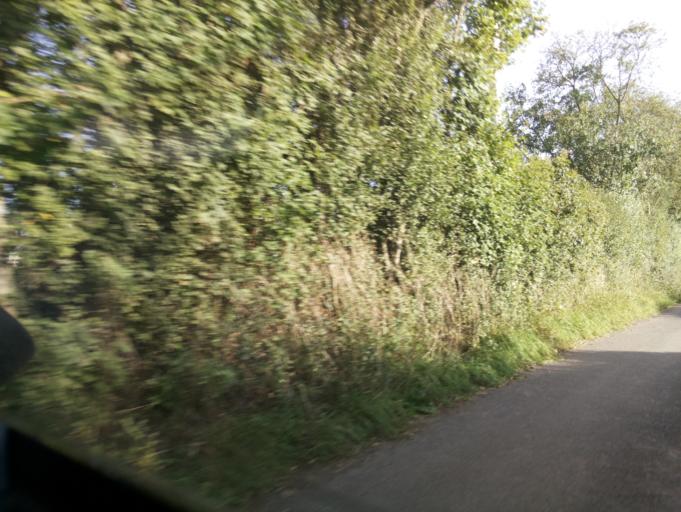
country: GB
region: England
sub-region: Gloucestershire
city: Newent
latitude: 51.9651
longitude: -2.3107
